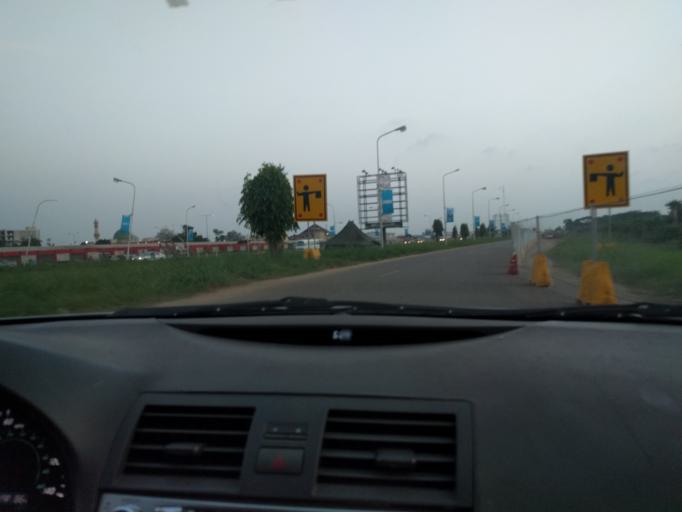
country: NG
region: Lagos
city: Oshodi
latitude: 6.5752
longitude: 3.3209
